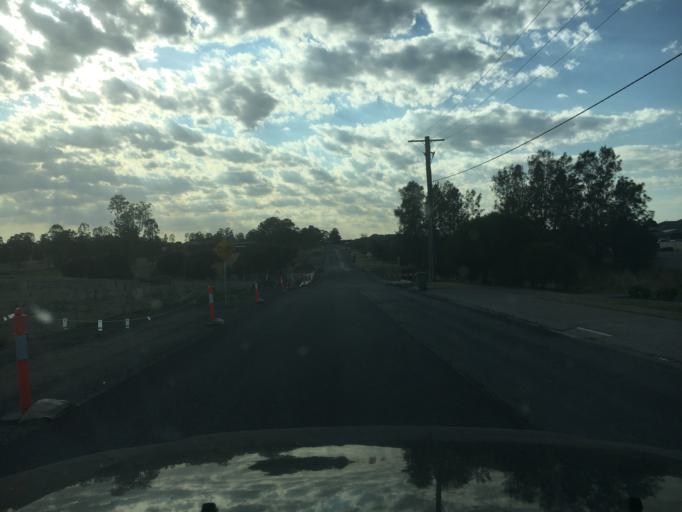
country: AU
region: New South Wales
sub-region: Cessnock
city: Branxton
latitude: -32.6514
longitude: 151.3661
